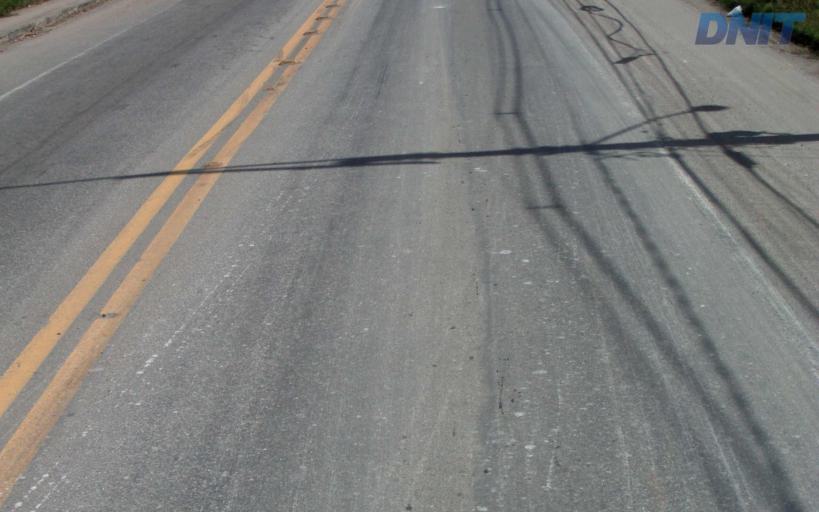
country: BR
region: Minas Gerais
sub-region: Coronel Fabriciano
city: Coronel Fabriciano
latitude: -19.5294
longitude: -42.6597
